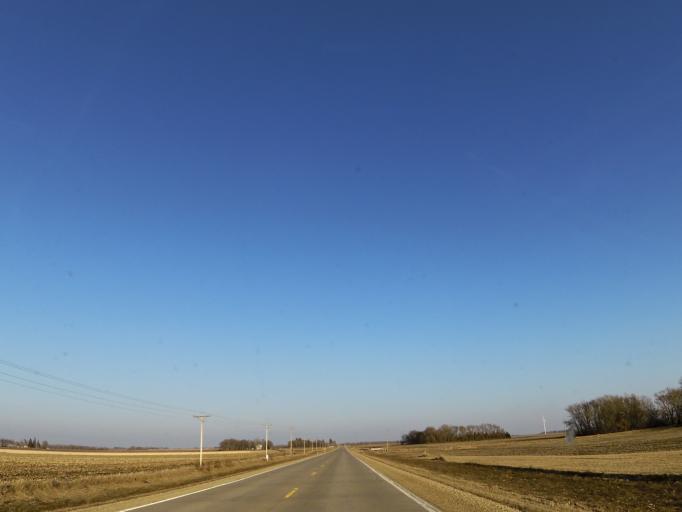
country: US
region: Iowa
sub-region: Worth County
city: Northwood
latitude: 43.4371
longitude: -93.0995
